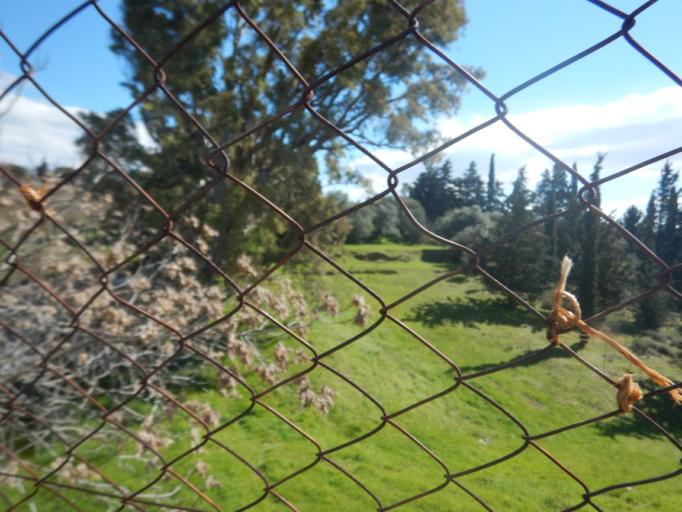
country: GR
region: Attica
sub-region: Nomarchia Athinas
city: Kifisia
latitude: 38.0656
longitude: 23.8200
